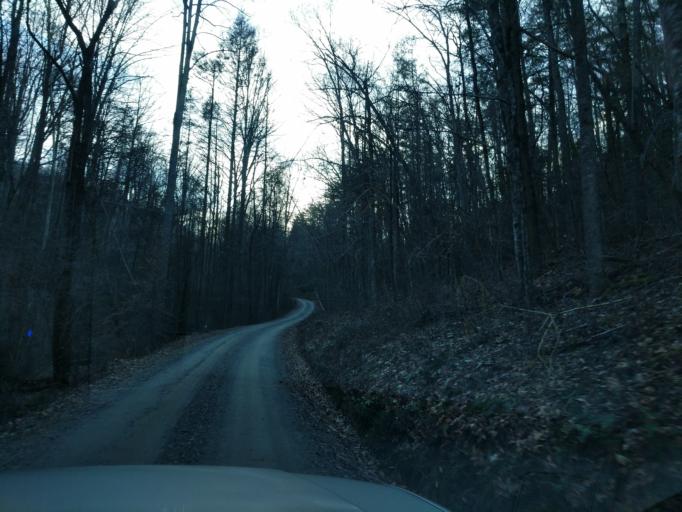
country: US
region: North Carolina
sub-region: Haywood County
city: Cove Creek
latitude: 35.7326
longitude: -83.0291
